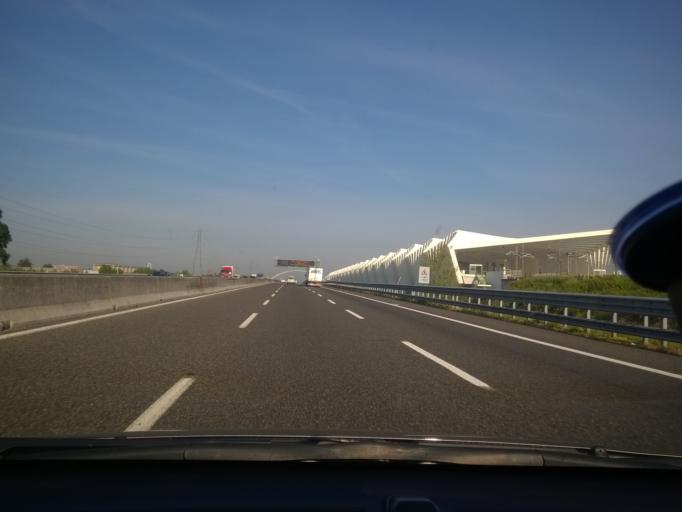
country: IT
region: Emilia-Romagna
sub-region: Provincia di Reggio Emilia
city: Reggio nell'Emilia
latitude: 44.7232
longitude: 10.6578
